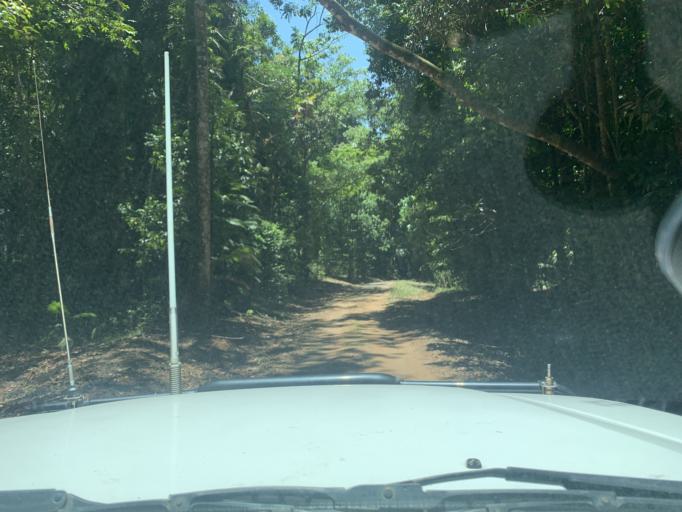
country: AU
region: Queensland
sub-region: Cairns
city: Redlynch
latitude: -16.9696
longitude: 145.6493
